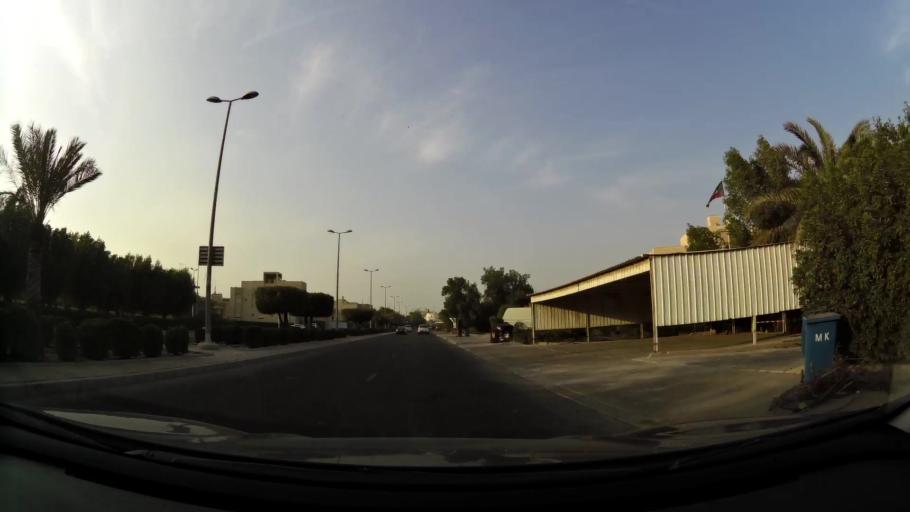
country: KW
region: Mubarak al Kabir
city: Sabah as Salim
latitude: 29.2549
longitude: 48.0707
